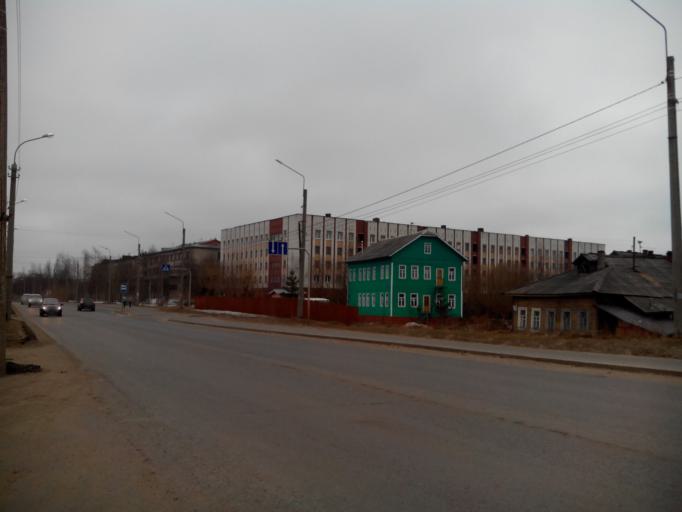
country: RU
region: Arkhangelskaya
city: Katunino
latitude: 64.5025
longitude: 40.6784
